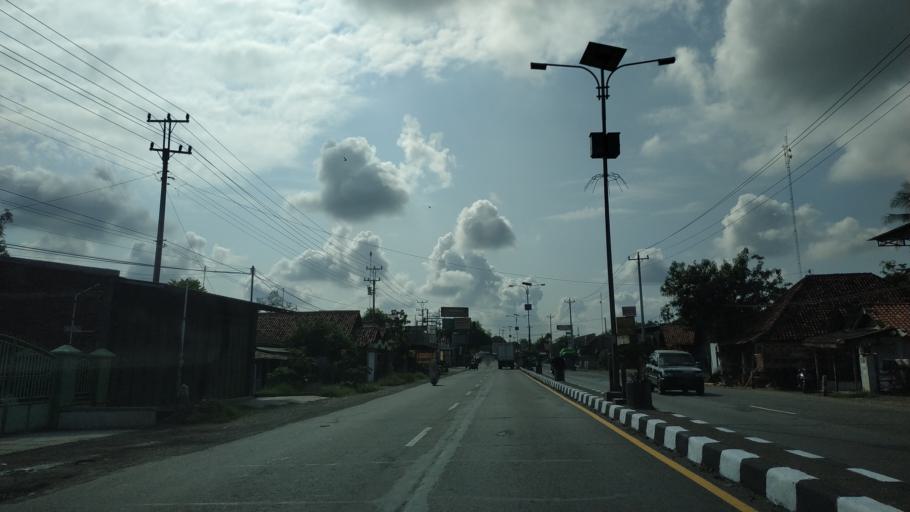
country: ID
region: Central Java
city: Comal
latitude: -6.9002
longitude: 109.5214
